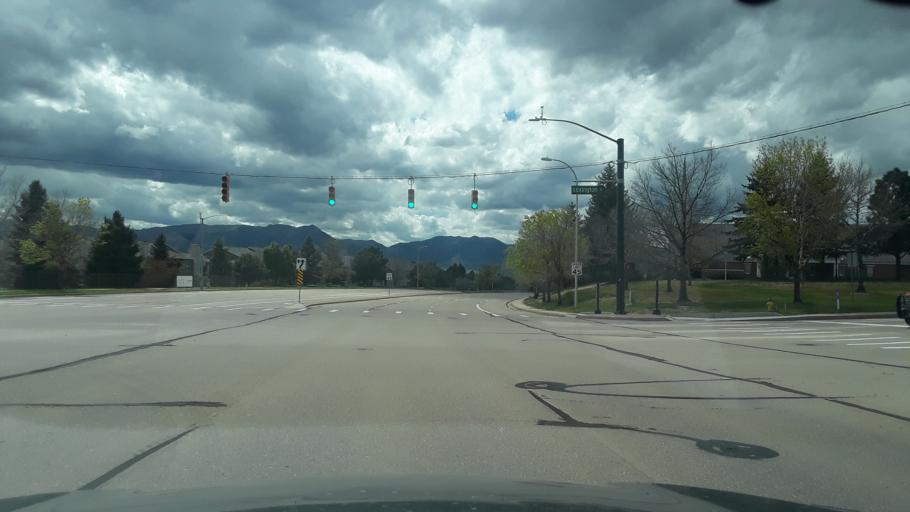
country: US
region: Colorado
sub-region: El Paso County
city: Black Forest
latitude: 38.9571
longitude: -104.7694
